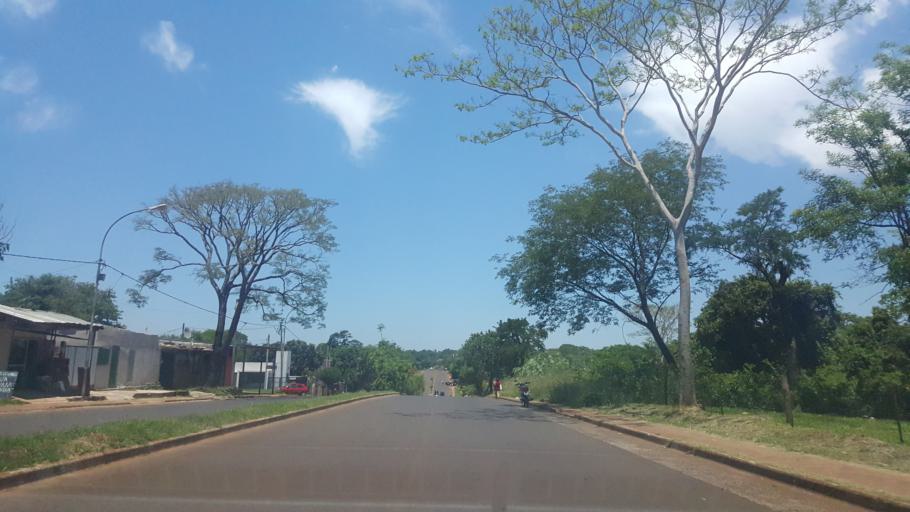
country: AR
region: Misiones
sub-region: Departamento de Capital
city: Posadas
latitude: -27.3607
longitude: -55.9385
